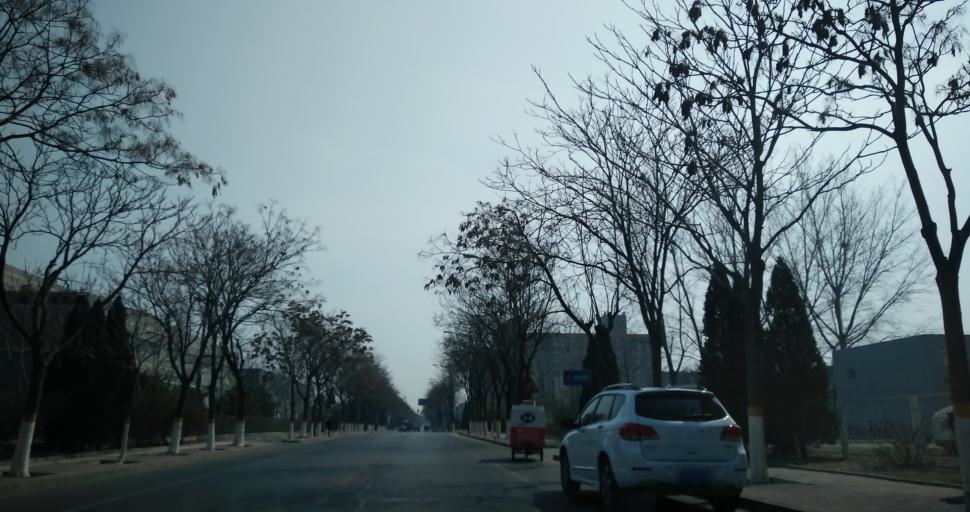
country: CN
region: Beijing
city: Jiugong
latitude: 39.7958
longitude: 116.5158
